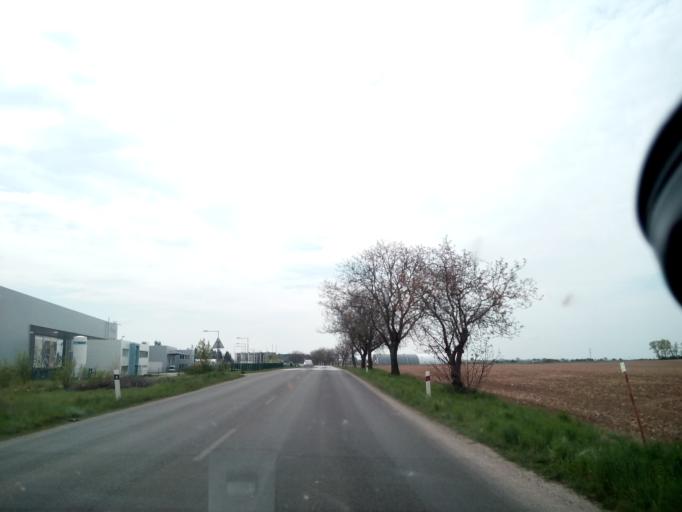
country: SK
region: Trnavsky
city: Vrbove
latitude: 48.6058
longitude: 17.7500
